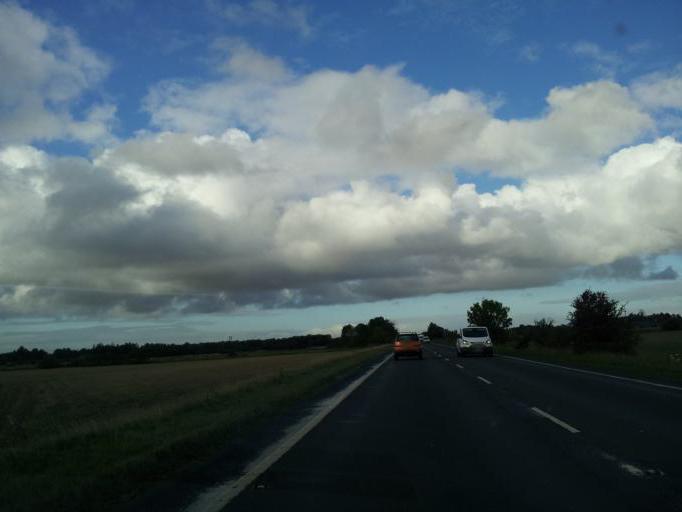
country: GB
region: England
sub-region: Norfolk
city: Terrington Saint John
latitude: 52.7507
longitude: 0.2430
